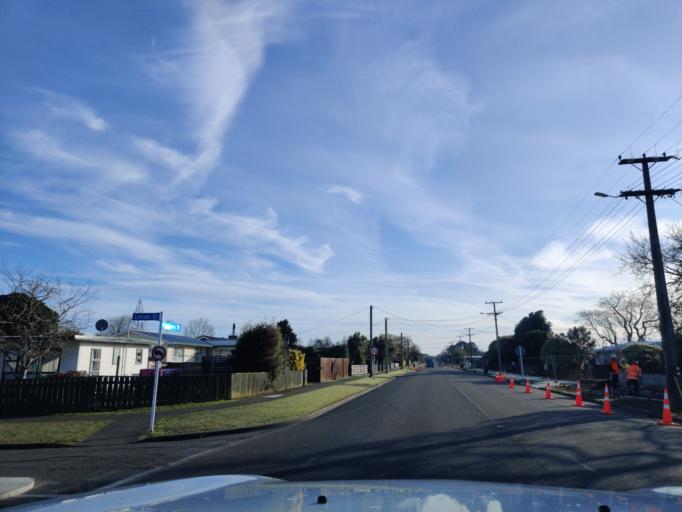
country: NZ
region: Manawatu-Wanganui
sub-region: Palmerston North City
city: Palmerston North
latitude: -40.2877
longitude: 175.7587
